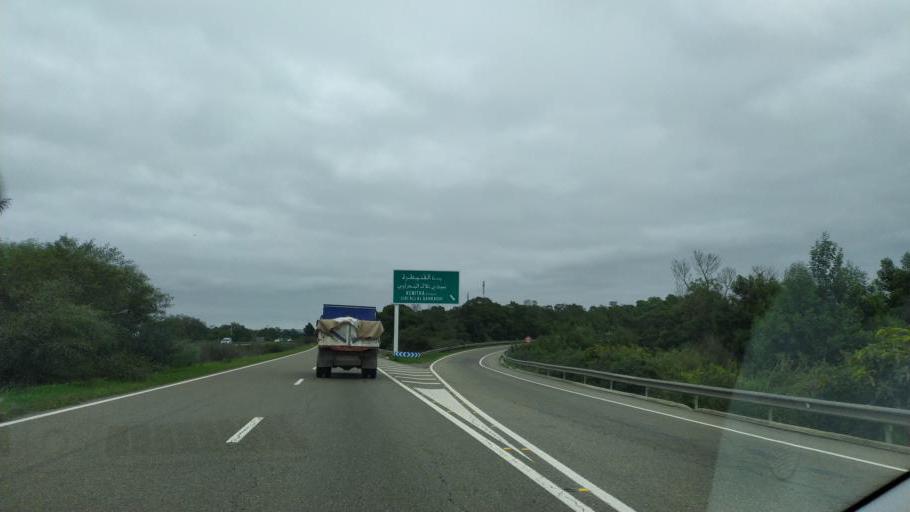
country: MA
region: Gharb-Chrarda-Beni Hssen
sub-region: Kenitra Province
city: Kenitra
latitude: 34.2296
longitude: -6.5763
